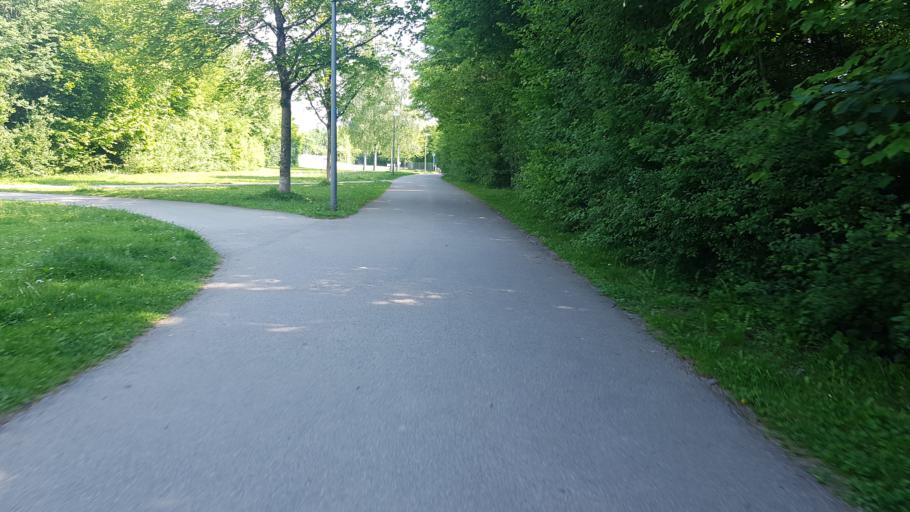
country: DE
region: Bavaria
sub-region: Upper Bavaria
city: Unterfoehring
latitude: 48.1740
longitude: 11.6412
